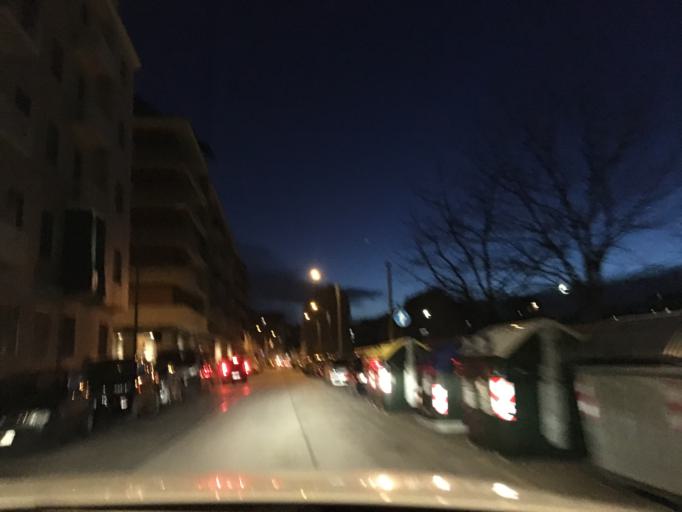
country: IT
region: Piedmont
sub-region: Provincia di Torino
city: Lesna
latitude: 45.0521
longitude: 7.6461
